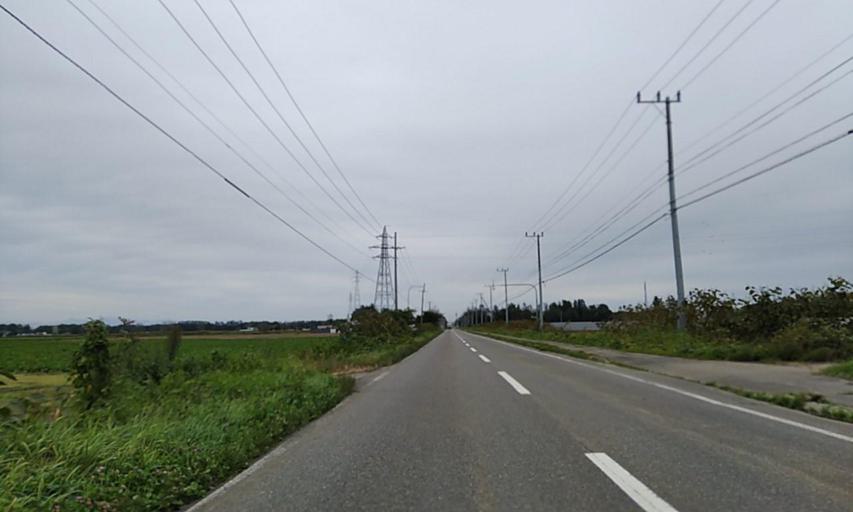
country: JP
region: Hokkaido
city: Obihiro
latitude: 42.6818
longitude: 143.1212
